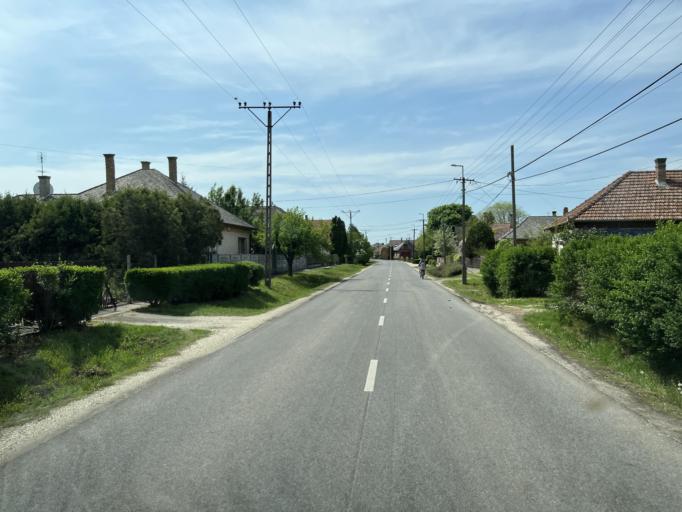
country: HU
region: Pest
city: Abony
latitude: 47.1942
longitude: 20.0116
